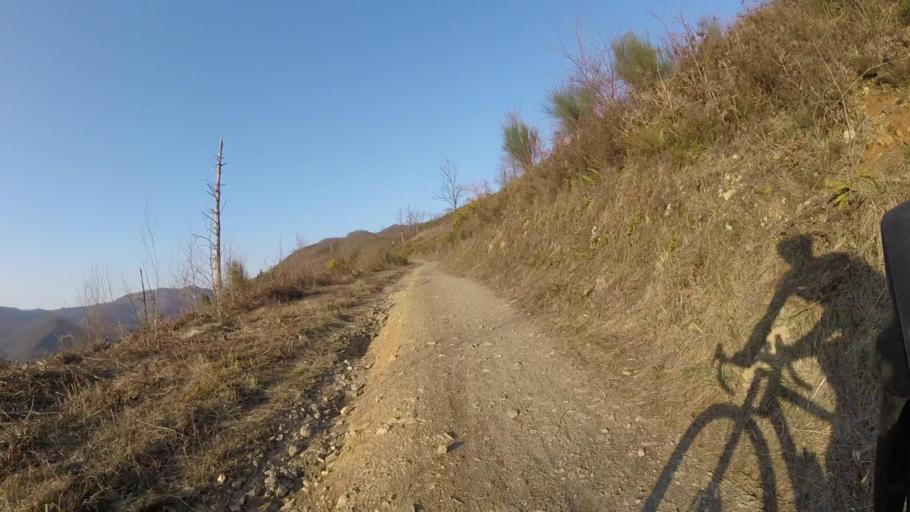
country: ES
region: Navarre
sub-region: Provincia de Navarra
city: Arano
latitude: 43.2208
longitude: -1.8605
